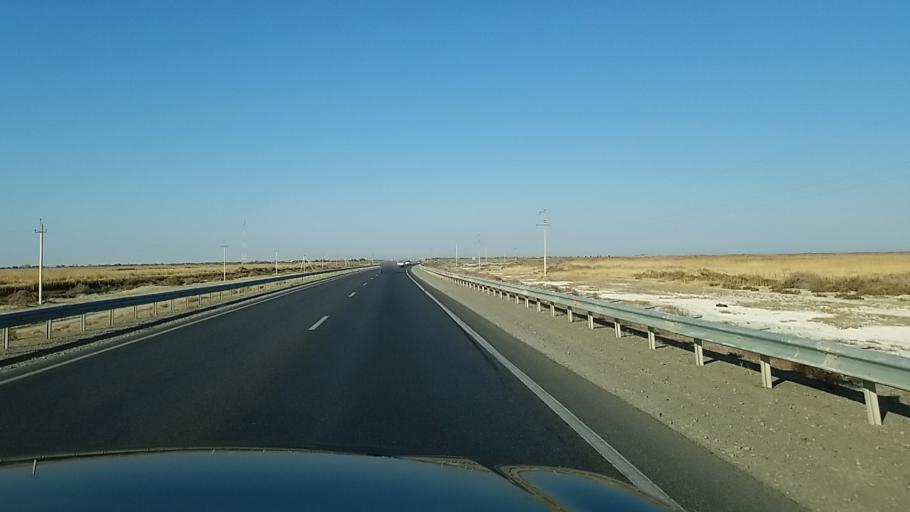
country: KZ
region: Qyzylorda
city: Terenozek
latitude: 44.8943
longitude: 65.0153
